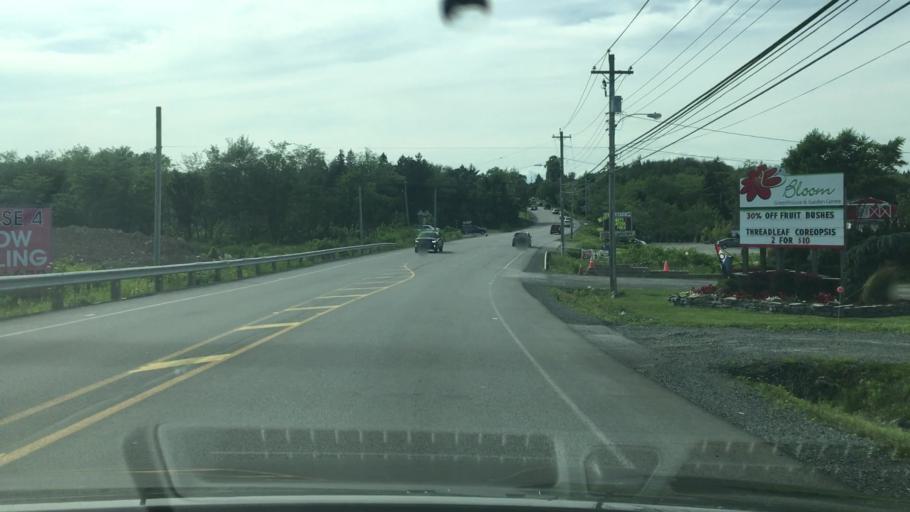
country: CA
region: Nova Scotia
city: Dartmouth
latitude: 44.7284
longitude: -63.7486
